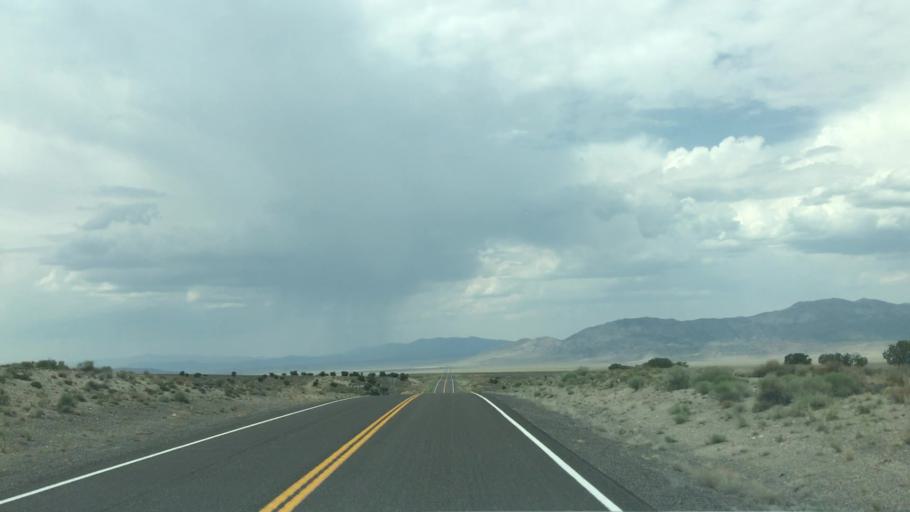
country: US
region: Nevada
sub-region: Eureka County
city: Eureka
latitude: 39.3934
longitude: -115.7250
